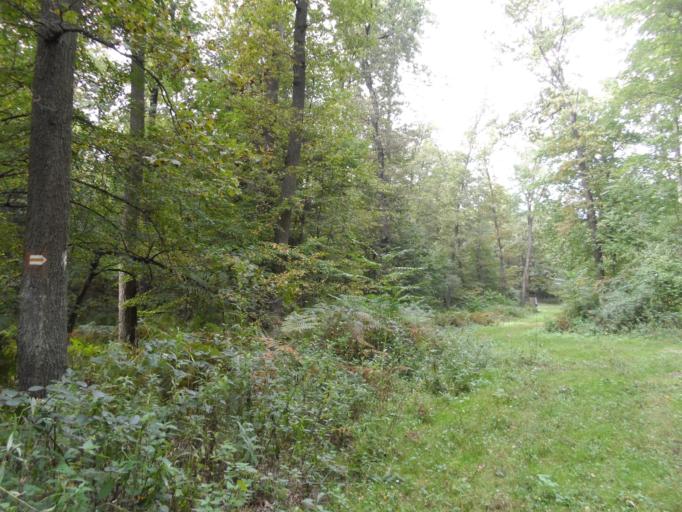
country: HU
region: Veszprem
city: Ajka
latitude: 47.2120
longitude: 17.5570
